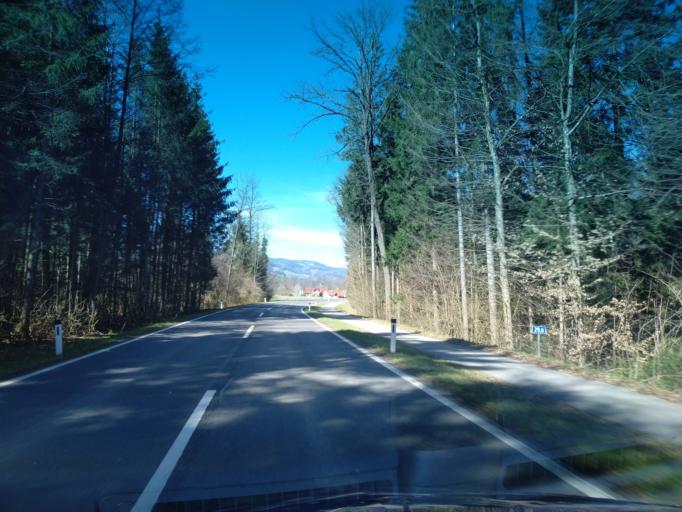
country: AT
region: Styria
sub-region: Politischer Bezirk Deutschlandsberg
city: Sankt Peter im Sulmtal
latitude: 46.7804
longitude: 15.2444
